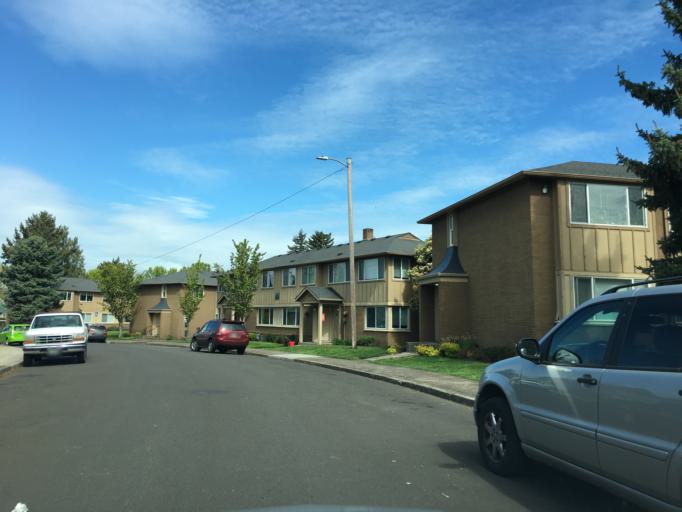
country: US
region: Oregon
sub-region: Multnomah County
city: Lents
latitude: 45.5357
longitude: -122.5952
